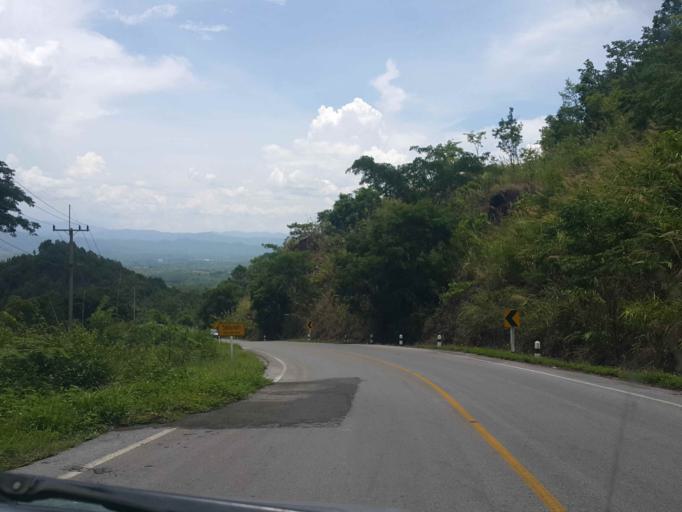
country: TH
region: Phayao
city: Chiang Muan
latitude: 18.9205
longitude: 100.1969
